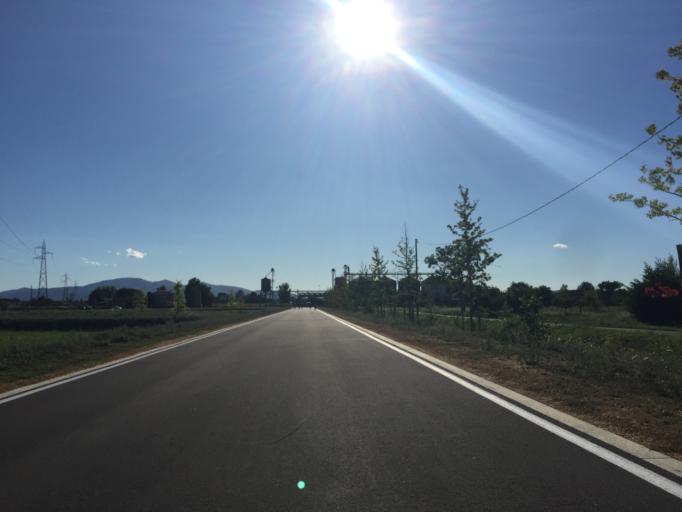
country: IT
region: Tuscany
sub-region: Provincia di Pistoia
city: Anchione
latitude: 43.8417
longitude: 10.7644
